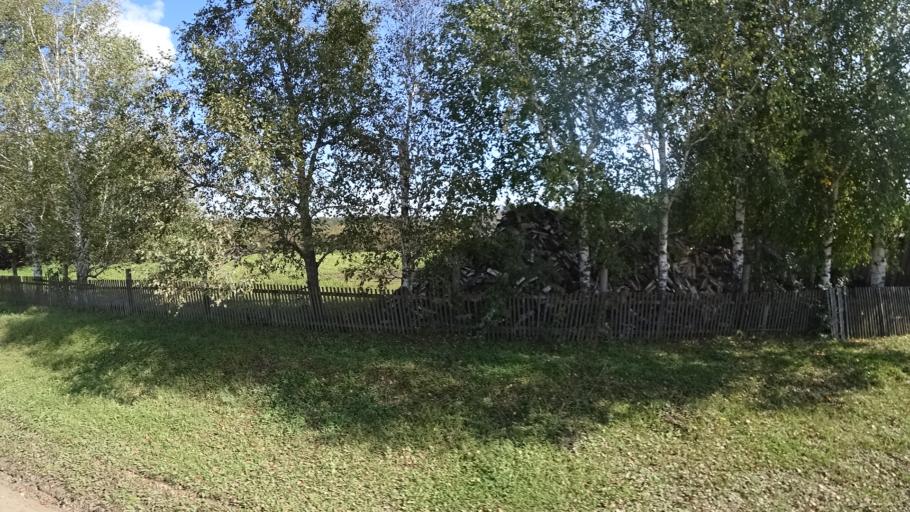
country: RU
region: Amur
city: Arkhara
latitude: 49.4041
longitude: 130.1532
